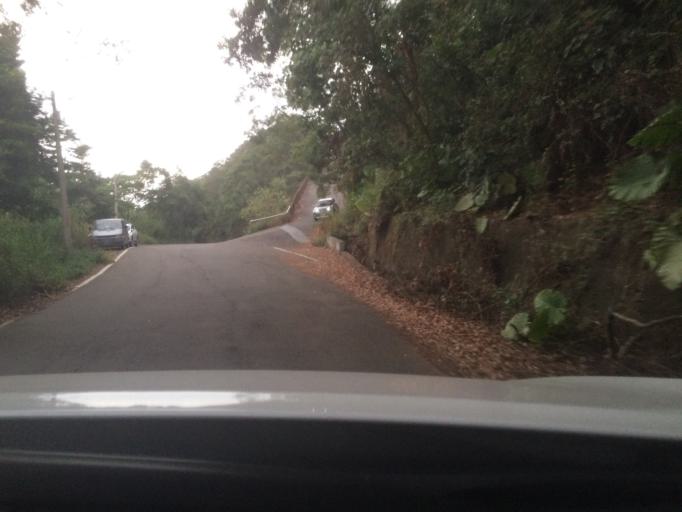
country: TW
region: Taiwan
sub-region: Nantou
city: Nantou
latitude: 23.9307
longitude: 120.6354
